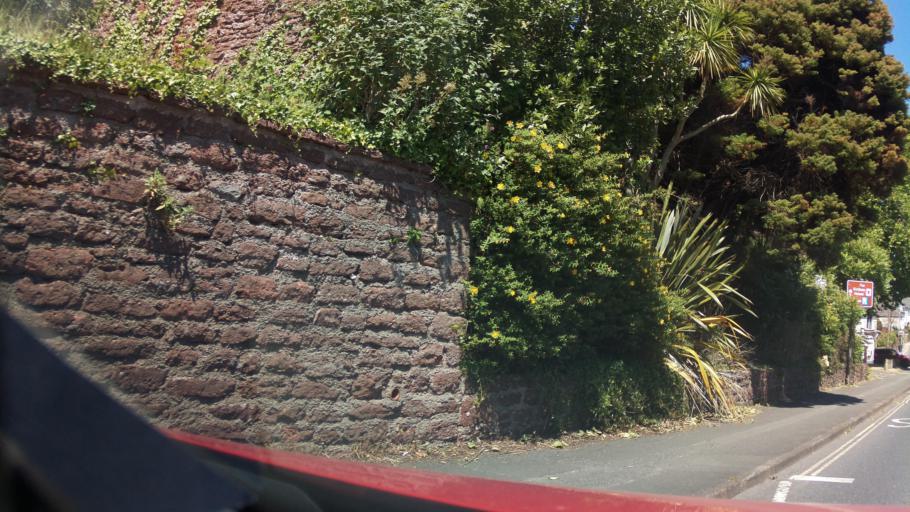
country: GB
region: England
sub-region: Borough of Torbay
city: Paignton
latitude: 50.4386
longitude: -3.5717
